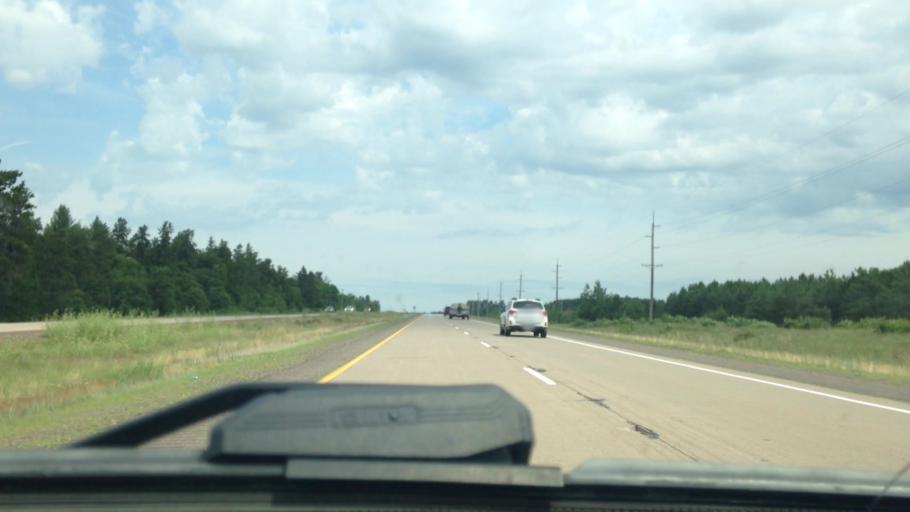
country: US
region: Wisconsin
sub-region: Douglas County
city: Lake Nebagamon
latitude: 46.2297
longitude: -91.8002
